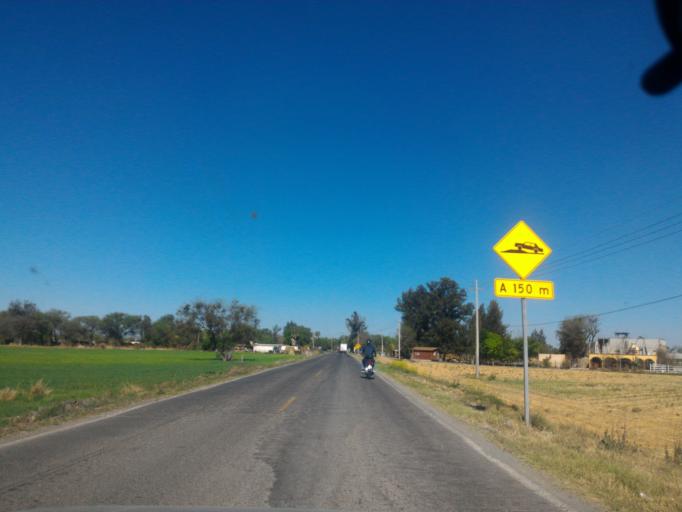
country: MX
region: Guanajuato
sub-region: San Francisco del Rincon
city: San Roque de Montes
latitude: 20.9989
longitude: -101.8094
